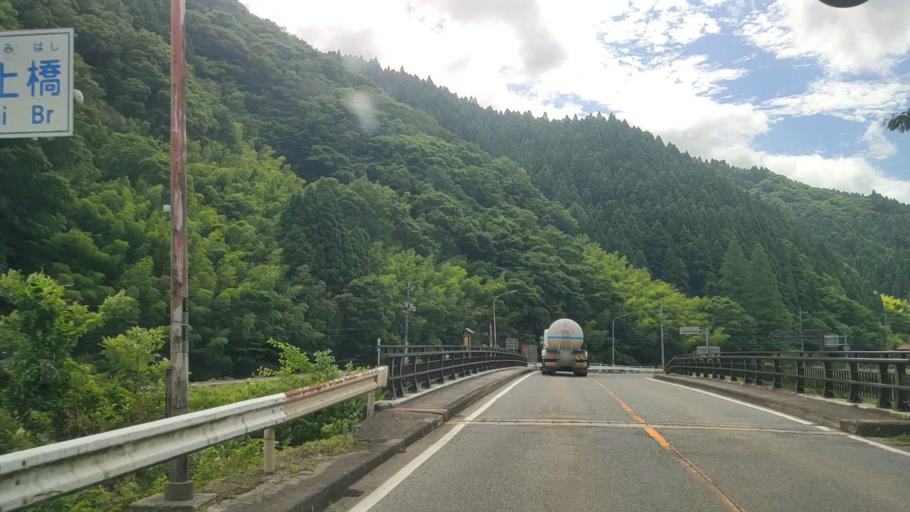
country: JP
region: Tottori
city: Yonago
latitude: 35.2312
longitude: 133.4415
